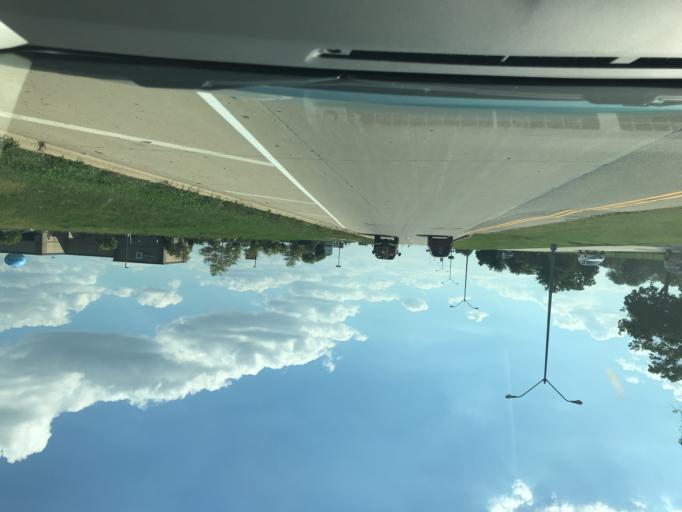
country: US
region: Wisconsin
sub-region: Walworth County
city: Delavan
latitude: 42.6280
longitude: -88.6026
